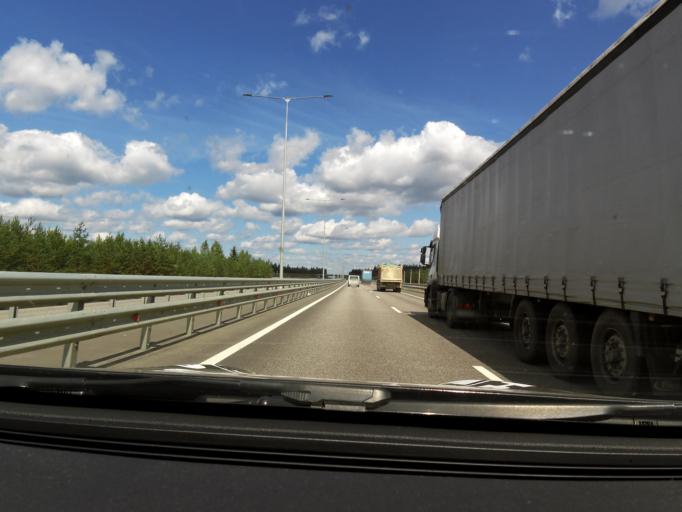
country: RU
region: Tverskaya
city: Krasnomayskiy
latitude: 57.5497
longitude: 34.2696
